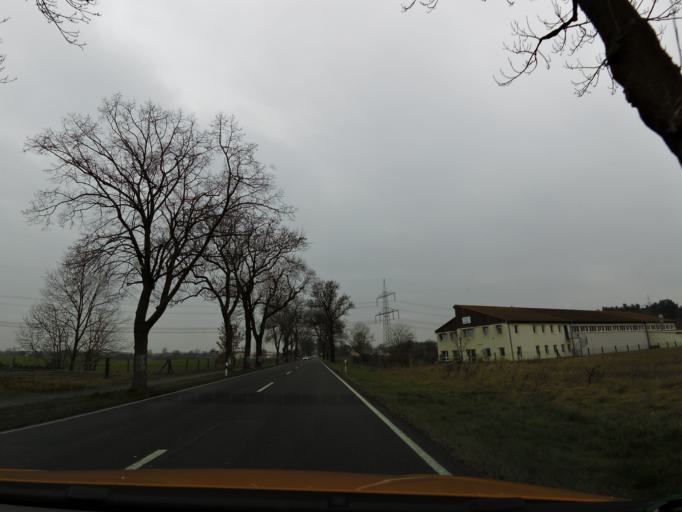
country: DE
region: Brandenburg
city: Gross Kreutz
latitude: 52.4002
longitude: 12.8026
